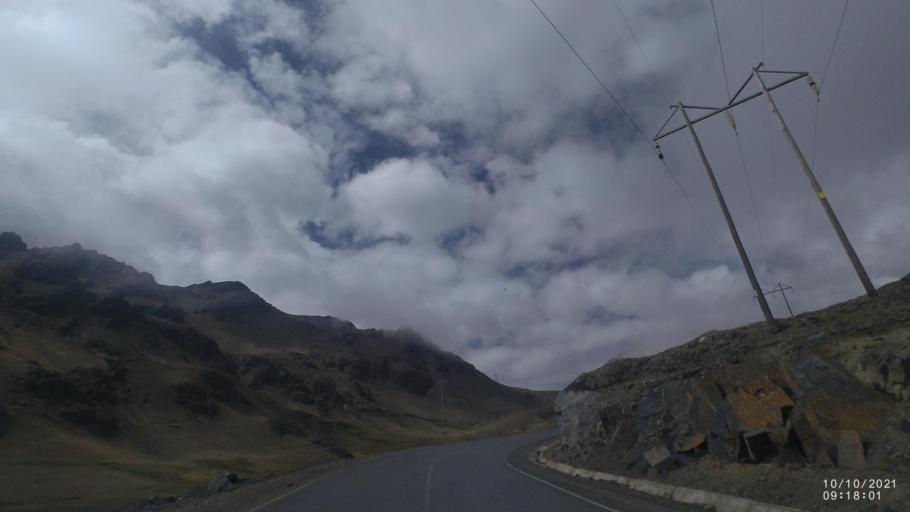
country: BO
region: La Paz
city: Quime
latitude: -17.0497
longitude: -67.2970
